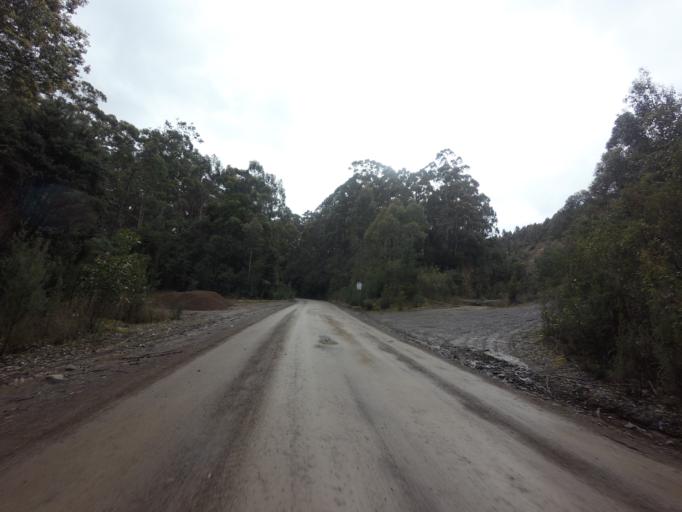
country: AU
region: Tasmania
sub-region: Huon Valley
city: Geeveston
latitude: -43.4998
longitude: 146.8785
